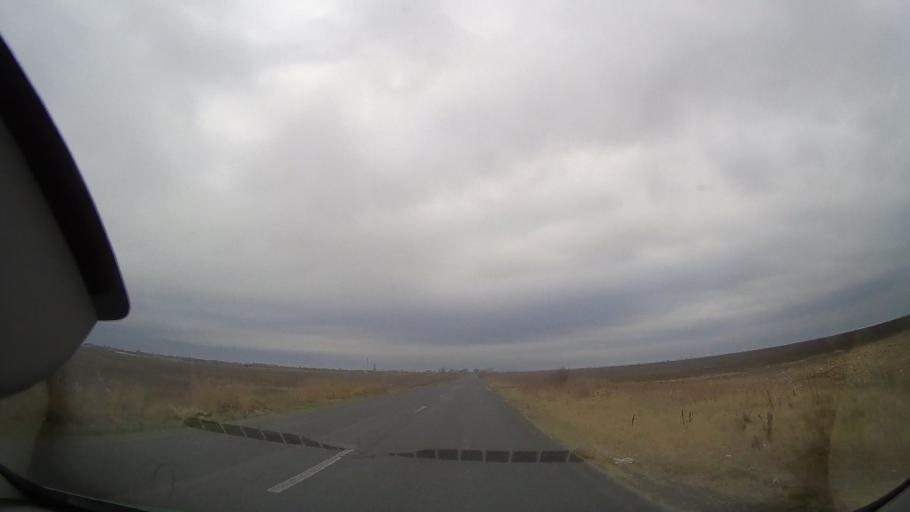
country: RO
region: Buzau
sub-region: Comuna Padina
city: Padina
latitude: 44.7891
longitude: 27.1450
